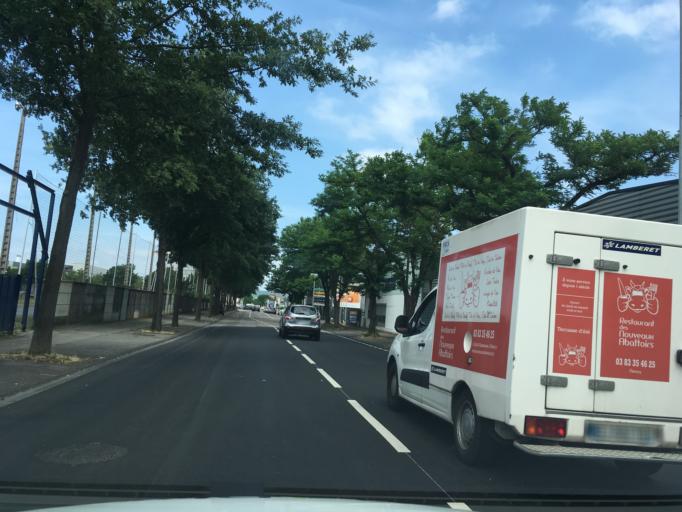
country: FR
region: Lorraine
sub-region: Departement de Meurthe-et-Moselle
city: Tomblaine
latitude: 48.6885
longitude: 6.2047
